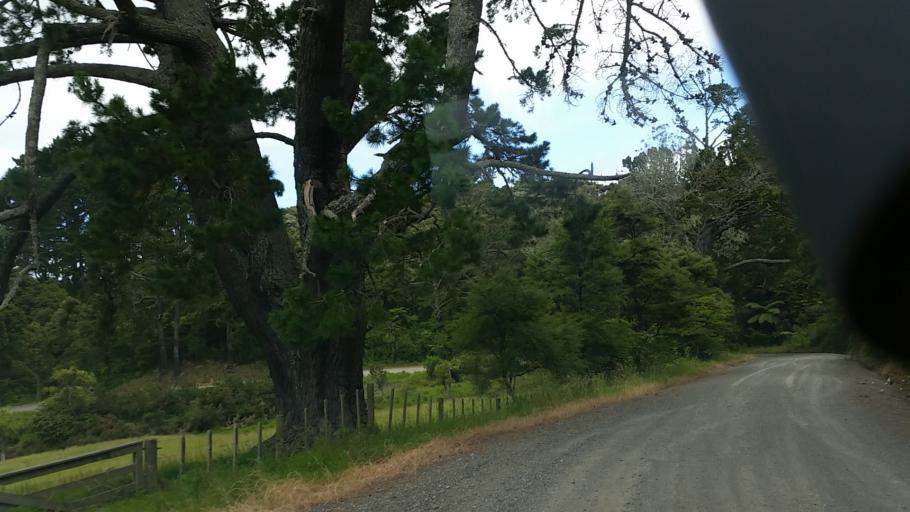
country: NZ
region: Auckland
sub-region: Auckland
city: Waitakere
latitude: -36.8753
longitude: 174.5805
